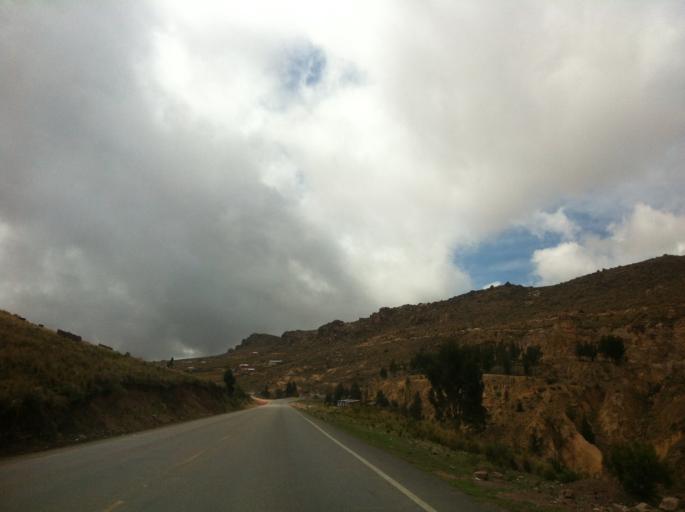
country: BO
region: Cochabamba
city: Irpa Irpa
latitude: -17.6994
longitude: -66.4791
